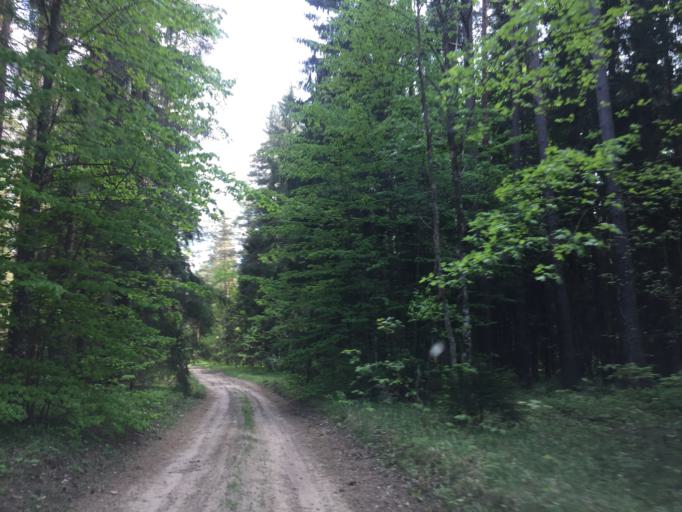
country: LV
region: Baldone
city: Baldone
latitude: 56.8027
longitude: 24.4268
